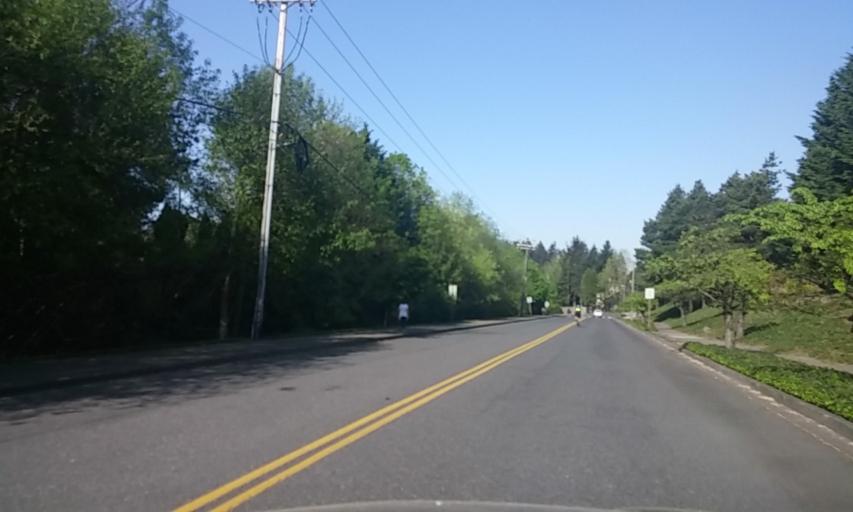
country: US
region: Oregon
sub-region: Washington County
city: Durham
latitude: 45.4261
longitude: -122.7310
